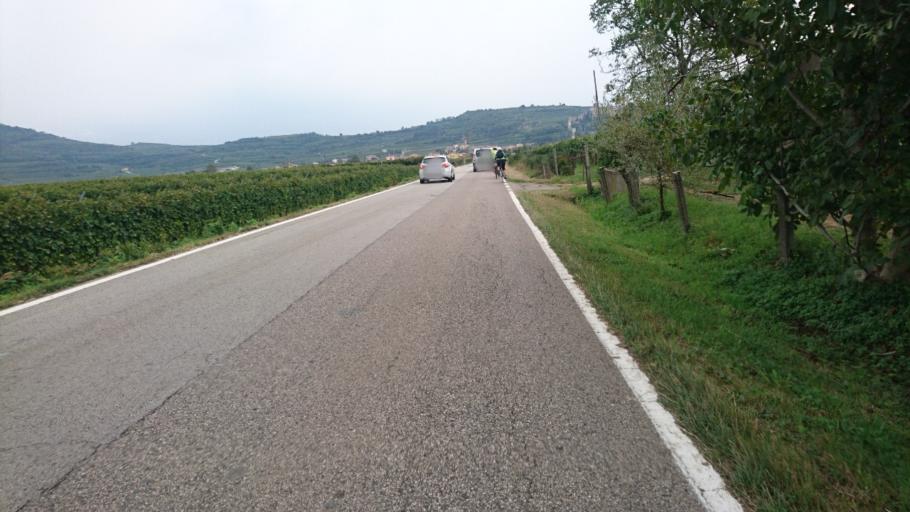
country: IT
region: Veneto
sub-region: Provincia di Verona
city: Soave
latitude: 45.4270
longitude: 11.2330
